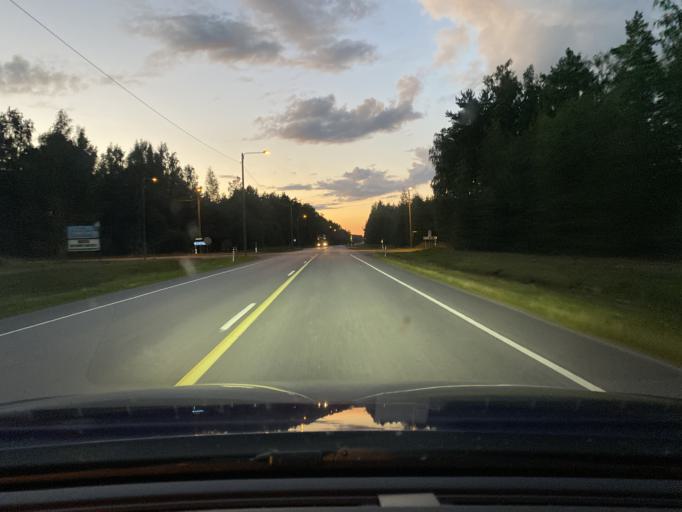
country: FI
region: Varsinais-Suomi
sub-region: Loimaa
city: Oripaeae
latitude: 60.9323
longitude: 22.6830
